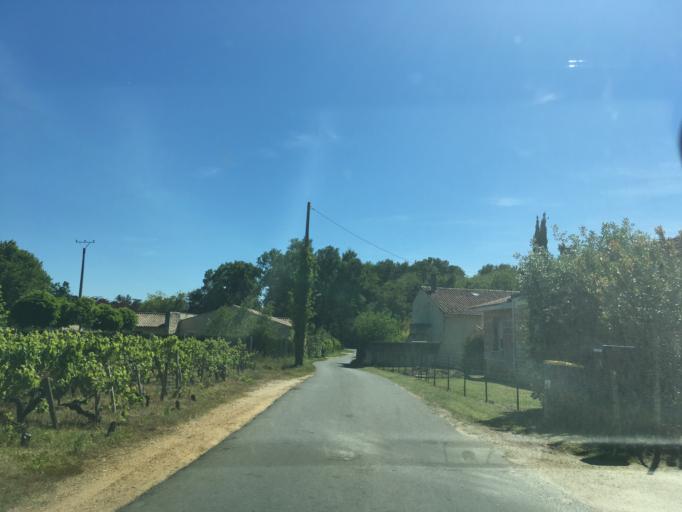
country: FR
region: Aquitaine
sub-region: Departement de la Gironde
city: Lesparre-Medoc
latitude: 45.2969
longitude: -0.8923
